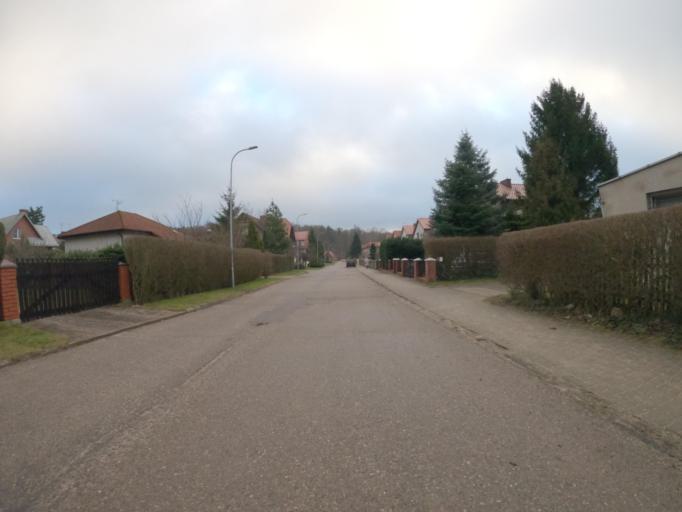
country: PL
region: West Pomeranian Voivodeship
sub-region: Koszalin
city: Koszalin
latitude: 54.2120
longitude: 16.2108
